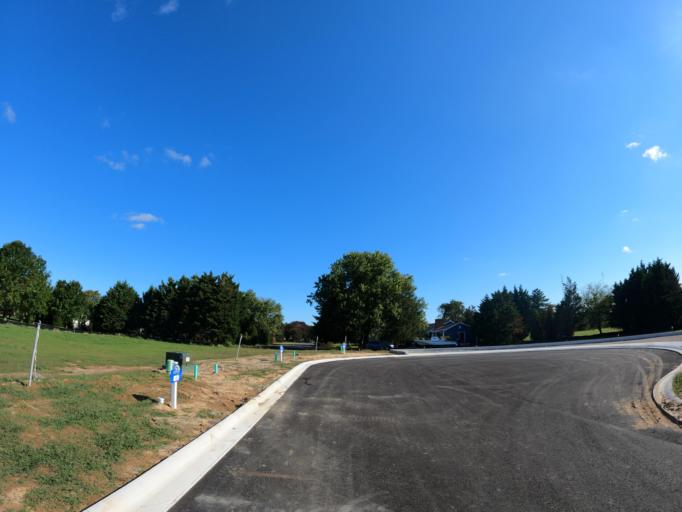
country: US
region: Delaware
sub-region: Sussex County
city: Lewes
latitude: 38.7562
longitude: -75.1611
